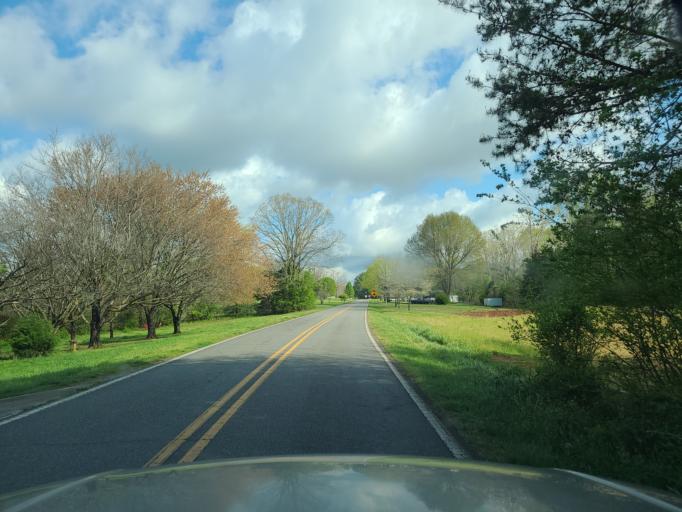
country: US
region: North Carolina
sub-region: Rutherford County
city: Forest City
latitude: 35.4333
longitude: -81.8324
